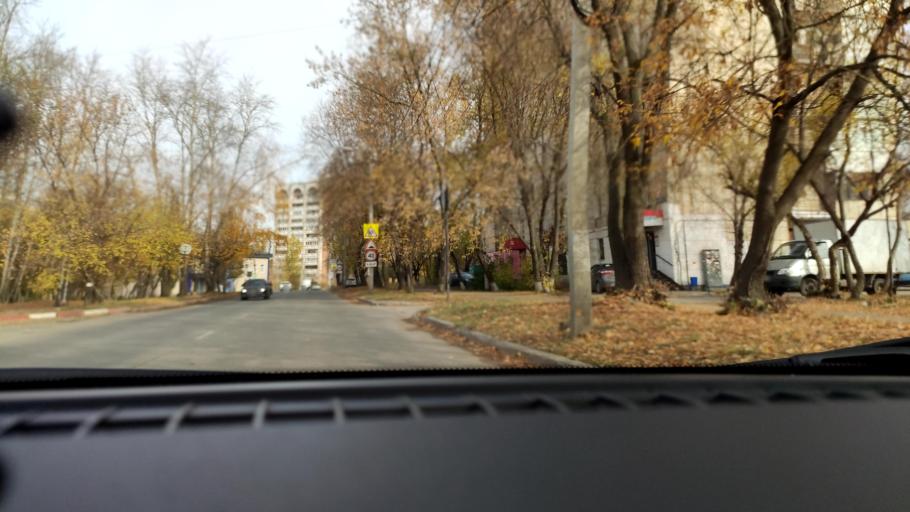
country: RU
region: Perm
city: Perm
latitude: 58.0653
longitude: 56.3550
